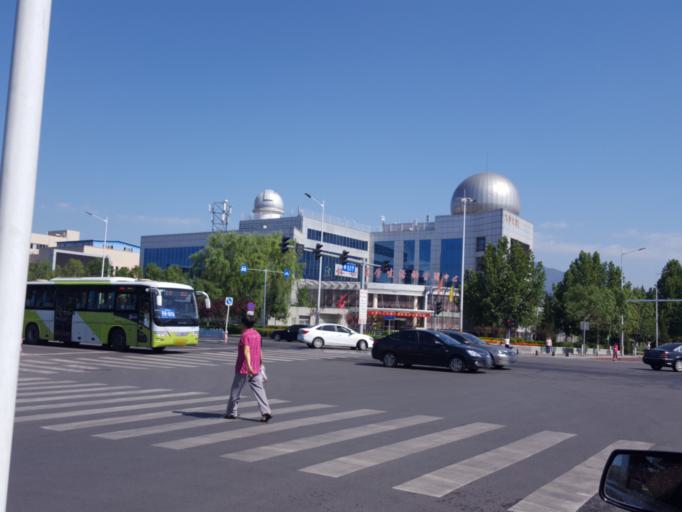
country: CN
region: Beijing
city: Longshan
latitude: 40.3341
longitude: 116.6331
